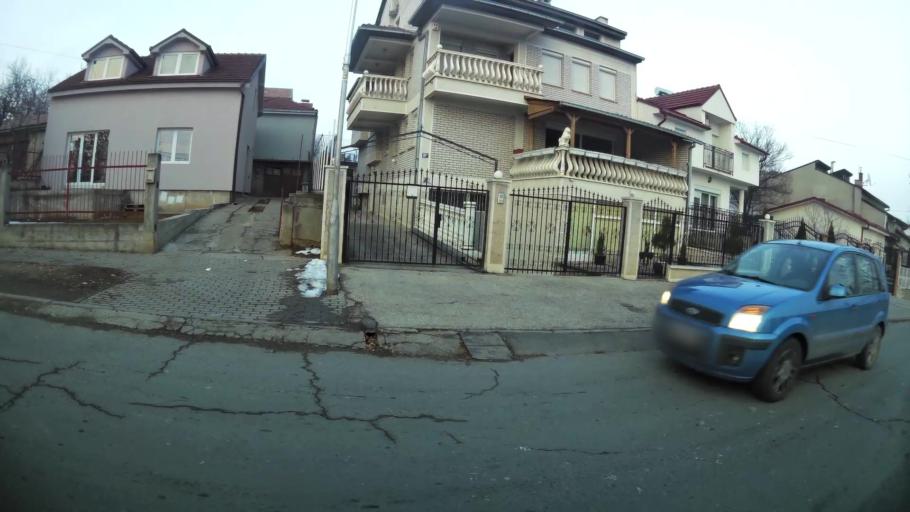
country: MK
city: Creshevo
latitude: 42.0103
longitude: 21.5070
